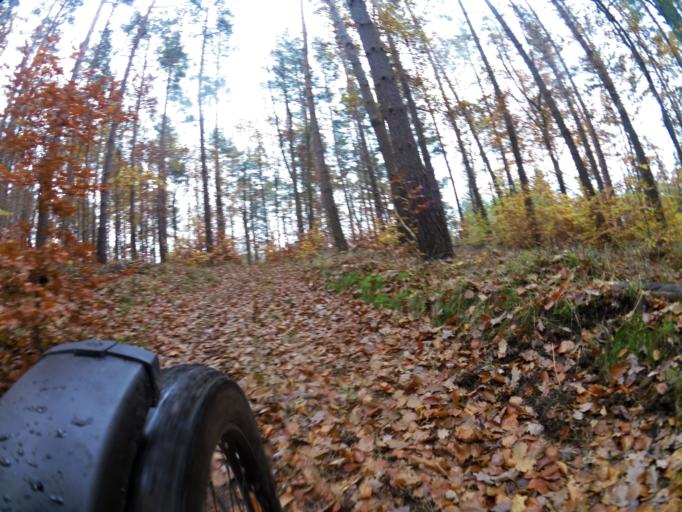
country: PL
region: Pomeranian Voivodeship
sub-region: Powiat pucki
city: Krokowa
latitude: 54.7450
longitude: 18.0955
